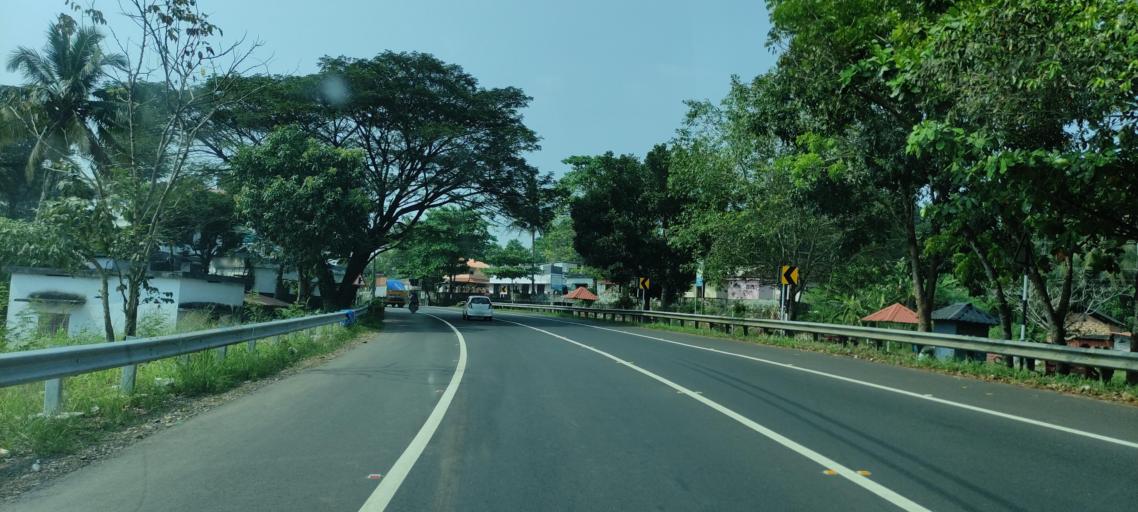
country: IN
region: Kerala
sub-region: Alappuzha
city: Chengannur
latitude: 9.2493
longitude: 76.6674
